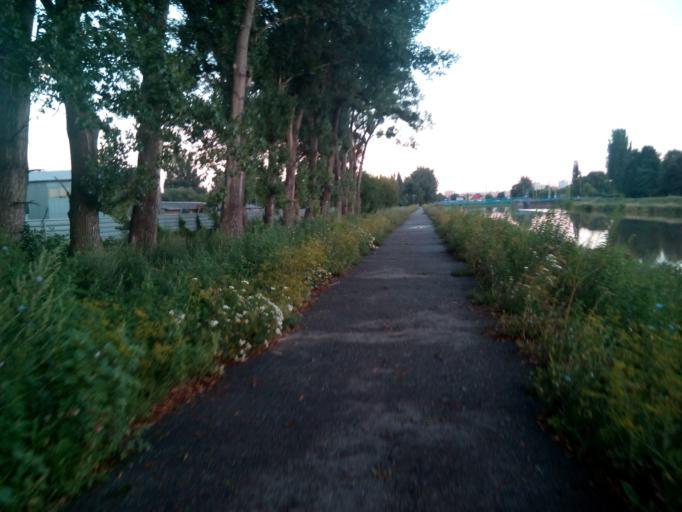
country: SK
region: Kosicky
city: Kosice
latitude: 48.7461
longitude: 21.2567
